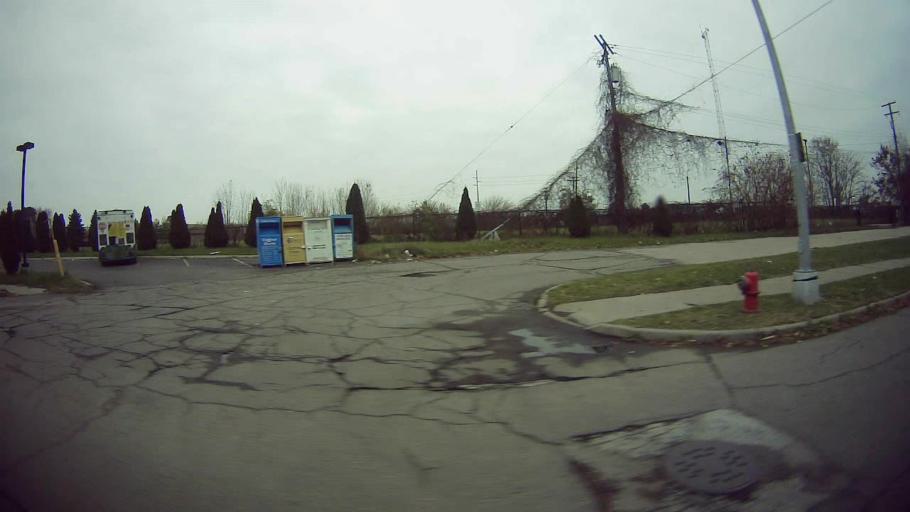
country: US
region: Michigan
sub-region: Wayne County
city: Hamtramck
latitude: 42.3952
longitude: -83.0475
